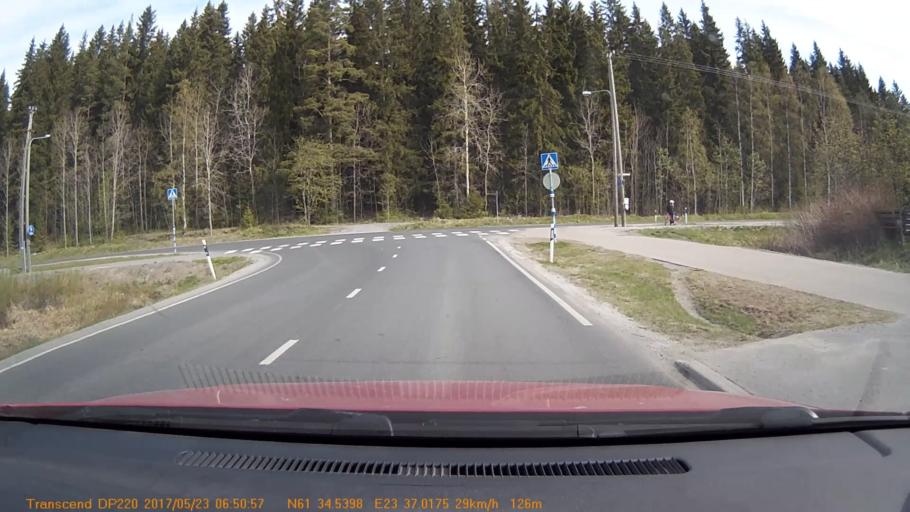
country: FI
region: Pirkanmaa
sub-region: Tampere
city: Yloejaervi
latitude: 61.5756
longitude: 23.6169
